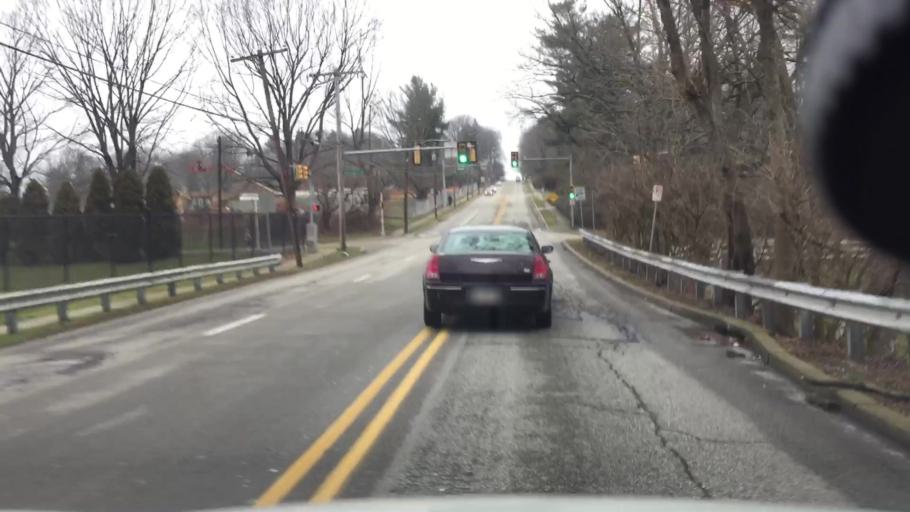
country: US
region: Pennsylvania
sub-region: Montgomery County
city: Flourtown
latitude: 40.0888
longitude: -75.2091
